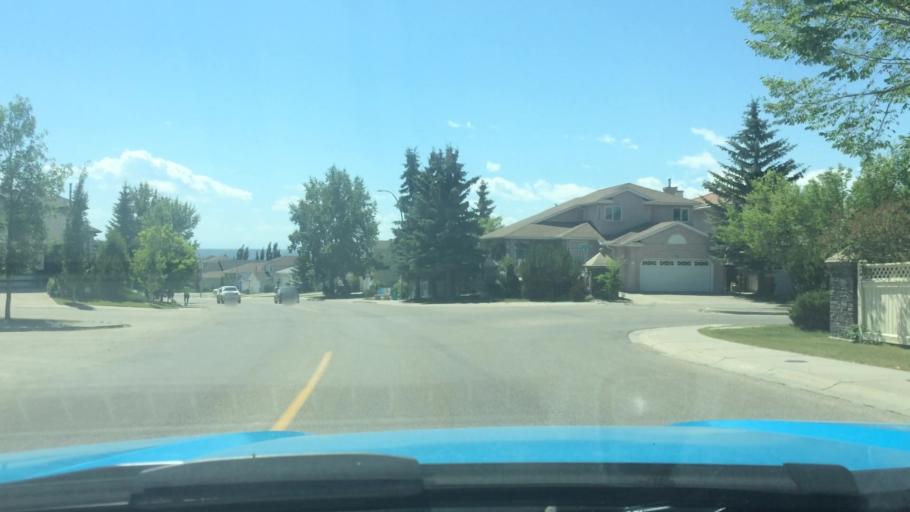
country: CA
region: Alberta
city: Calgary
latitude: 51.1369
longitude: -114.1908
